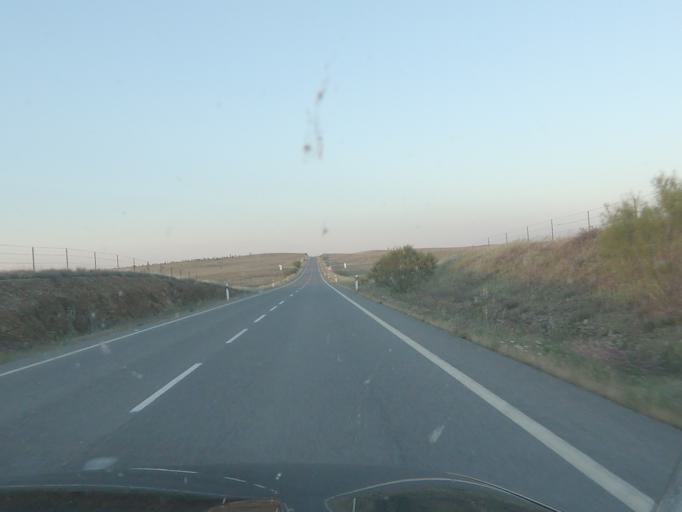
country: ES
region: Extremadura
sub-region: Provincia de Caceres
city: Salorino
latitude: 39.6079
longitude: -6.9684
